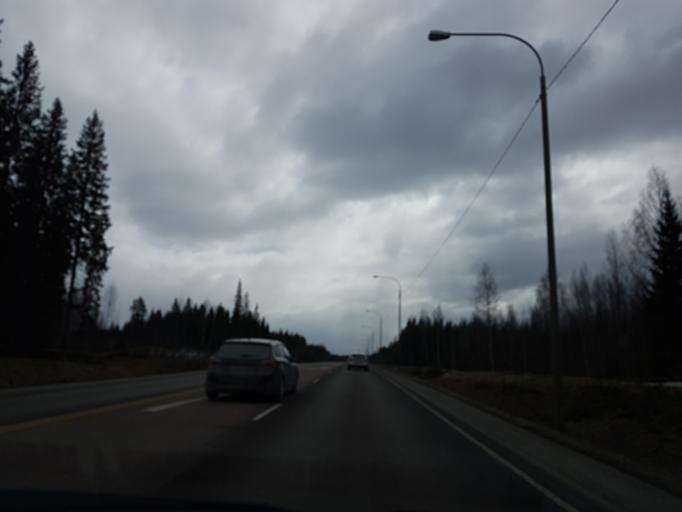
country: FI
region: Northern Savo
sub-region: Varkaus
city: Varkaus
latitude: 62.3723
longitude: 27.8096
